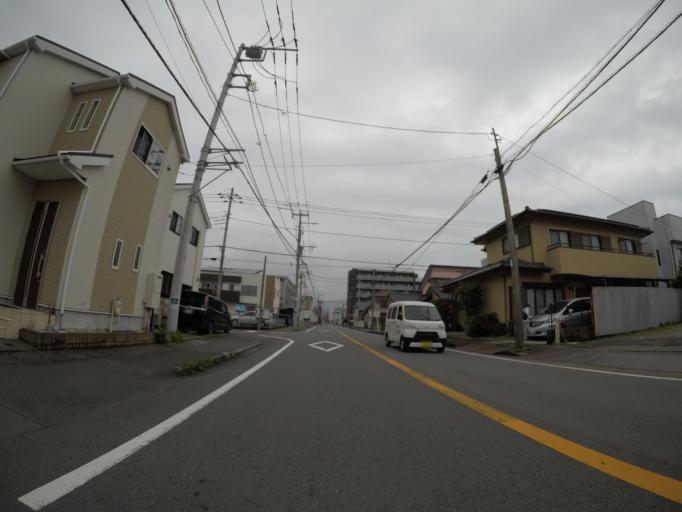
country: JP
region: Shizuoka
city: Numazu
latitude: 35.1100
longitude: 138.8519
